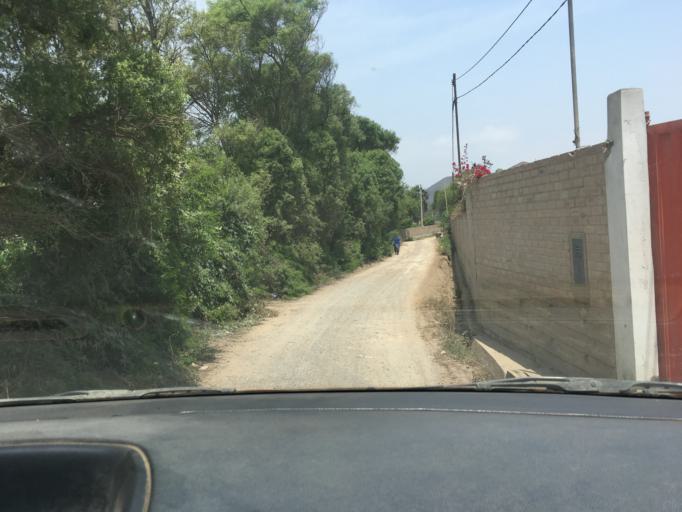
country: PE
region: Lima
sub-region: Lima
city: Cieneguilla
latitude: -12.1879
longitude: -76.8639
